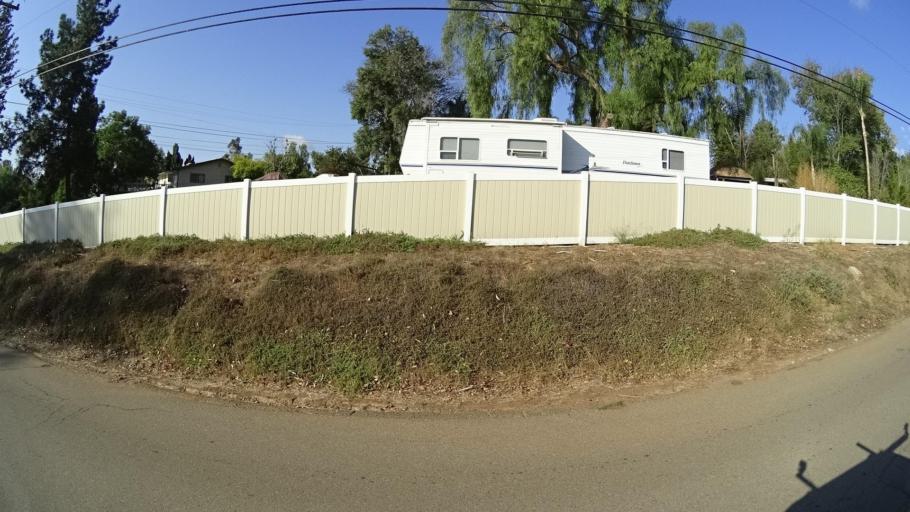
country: US
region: California
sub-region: San Diego County
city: Eucalyptus Hills
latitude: 32.8841
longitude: -116.9433
